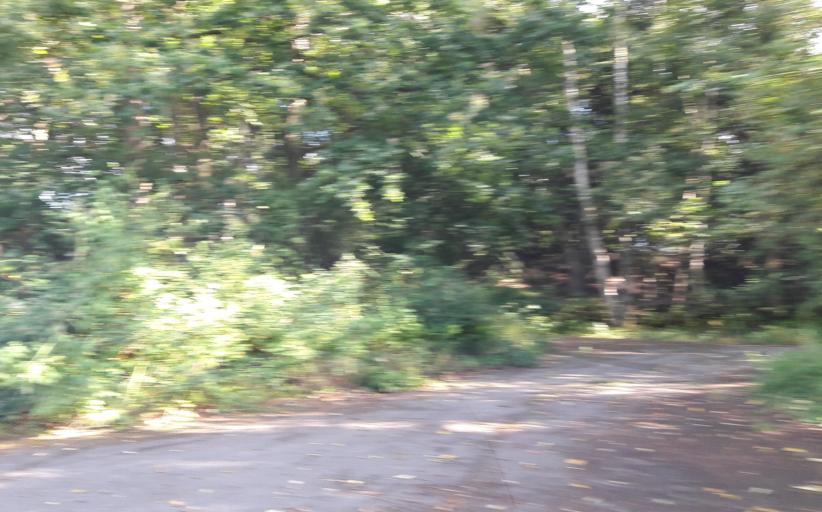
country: DE
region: Saarland
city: Bexbach
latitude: 49.3420
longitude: 7.2389
